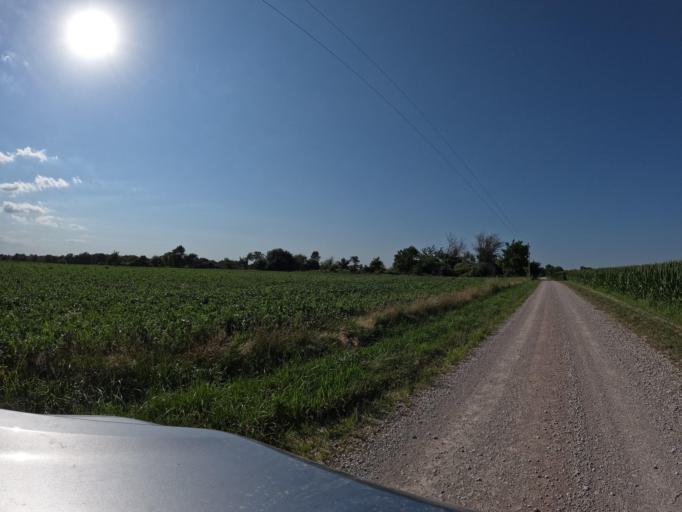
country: US
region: Iowa
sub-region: Appanoose County
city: Centerville
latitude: 40.7241
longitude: -93.0158
